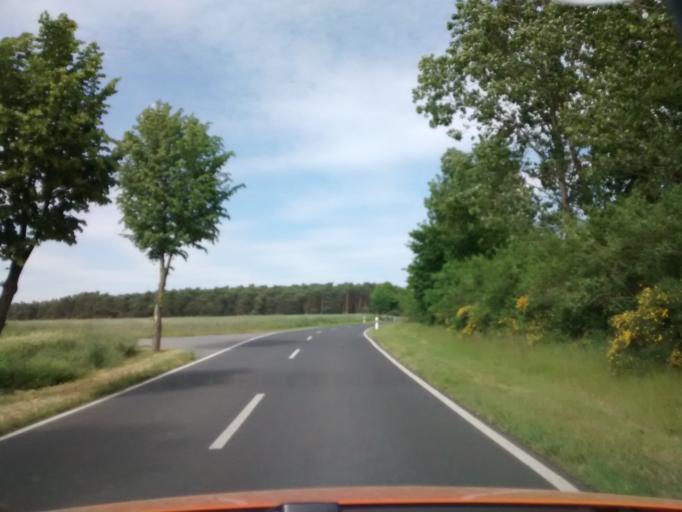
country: DE
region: Brandenburg
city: Ihlow
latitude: 51.9035
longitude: 13.3156
